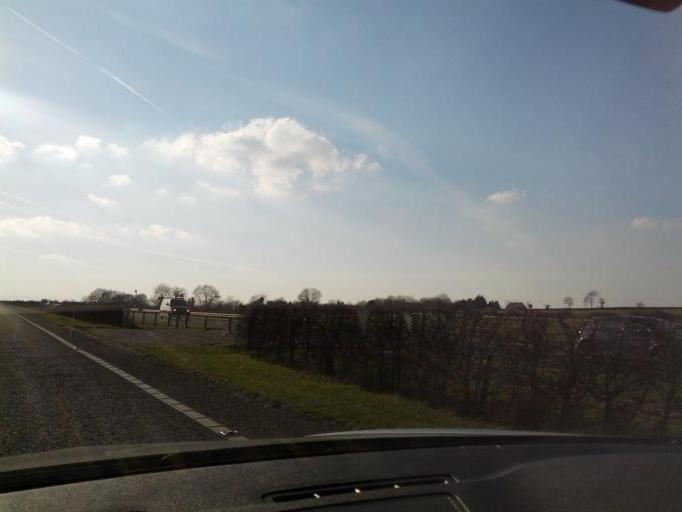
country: IE
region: Leinster
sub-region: Kildare
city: Cherryville
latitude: 53.1530
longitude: -6.9650
